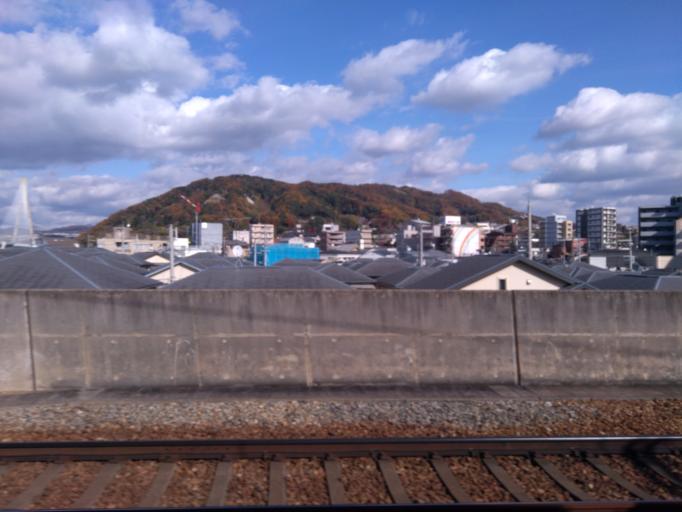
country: JP
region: Osaka
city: Ikeda
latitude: 34.8244
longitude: 135.4217
